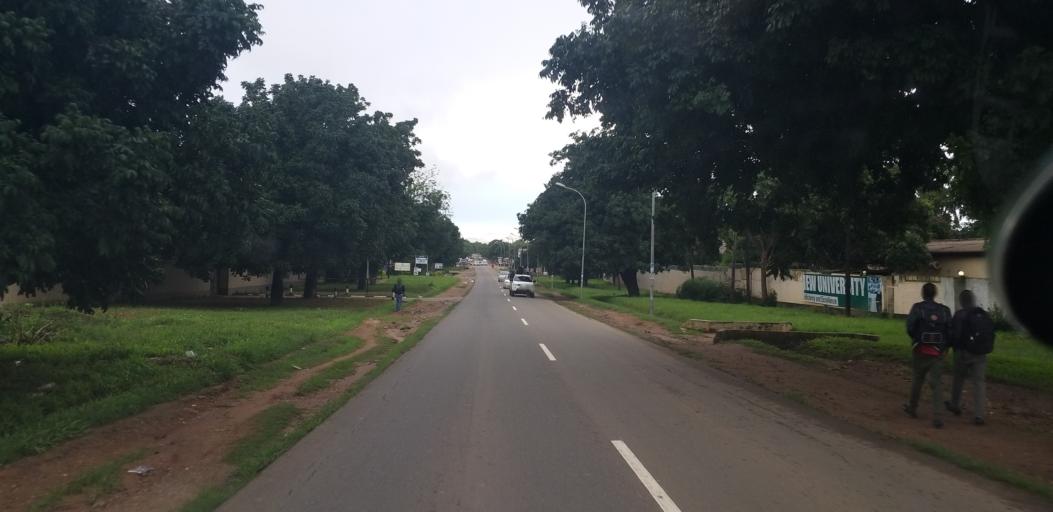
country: ZM
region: Lusaka
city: Lusaka
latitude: -15.4346
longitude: 28.3515
